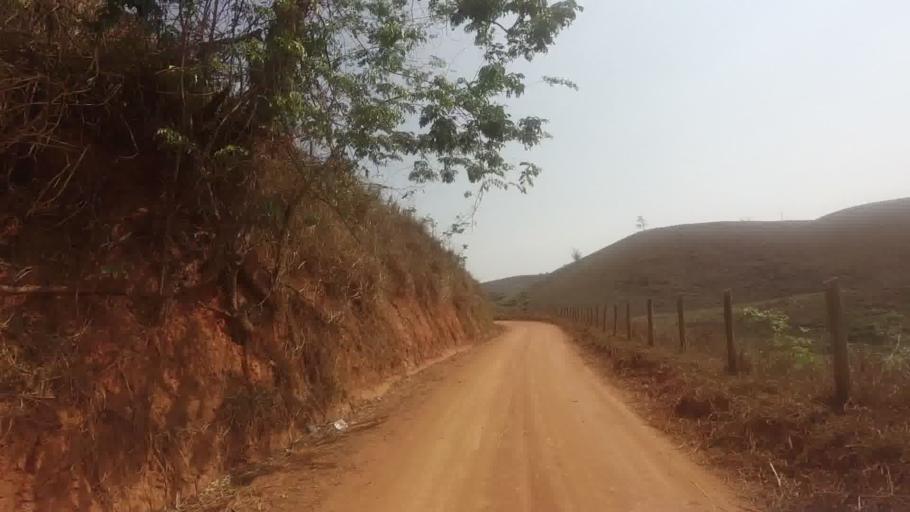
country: BR
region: Espirito Santo
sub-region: Sao Jose Do Calcado
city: Sao Jose do Calcado
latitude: -21.0663
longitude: -41.5466
